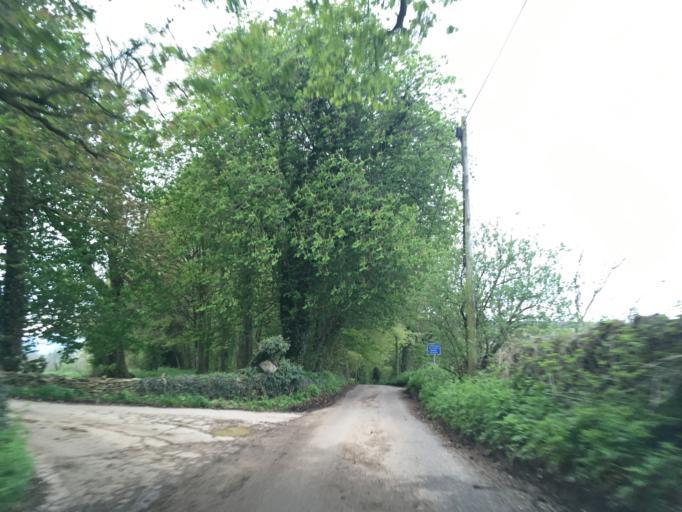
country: GB
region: England
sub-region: Gloucestershire
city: Wotton-under-Edge
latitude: 51.6398
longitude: -2.3311
